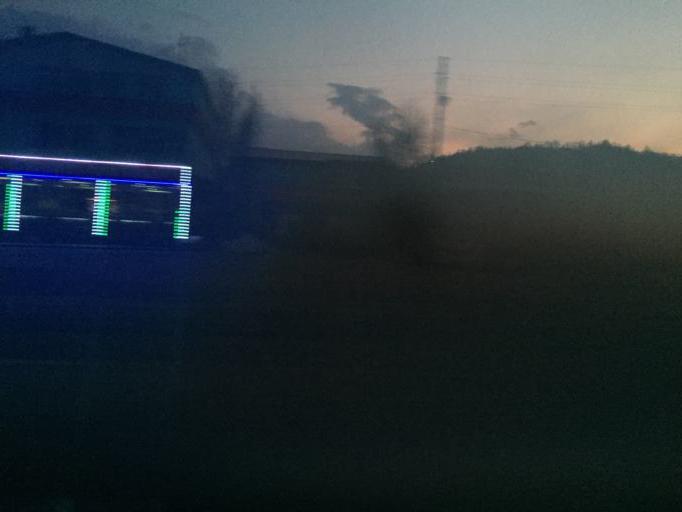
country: TR
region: Samsun
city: Kavak
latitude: 41.1358
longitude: 36.1265
